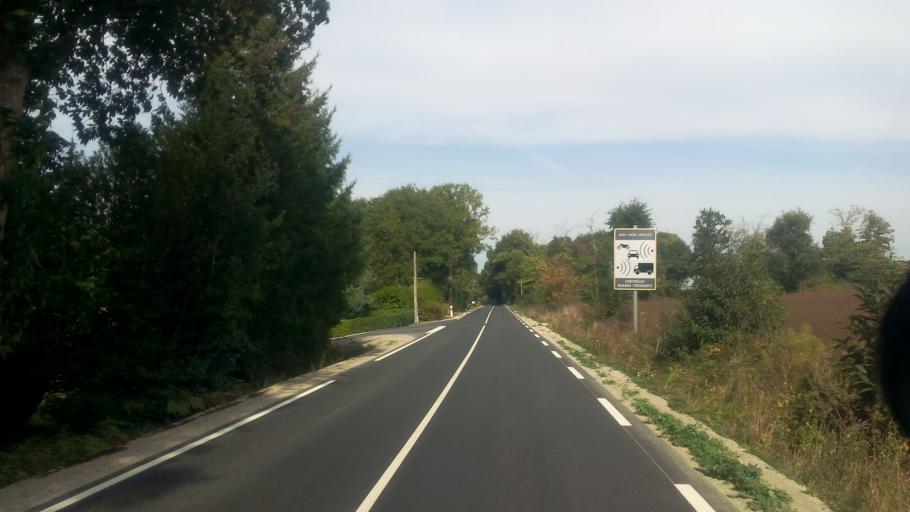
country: FR
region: Brittany
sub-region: Departement d'Ille-et-Vilaine
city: Bains-sur-Oust
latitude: 47.6924
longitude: -2.0849
